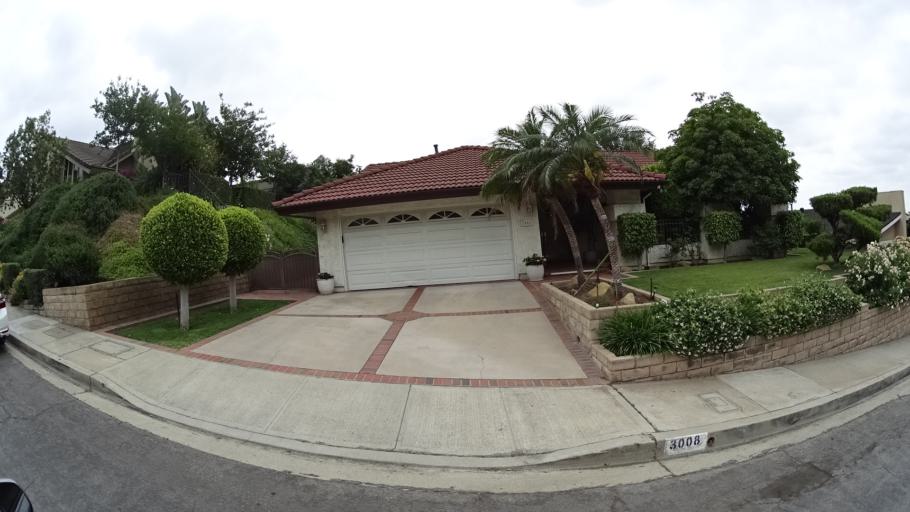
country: US
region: California
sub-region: Los Angeles County
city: Burbank
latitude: 34.2100
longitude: -118.3277
